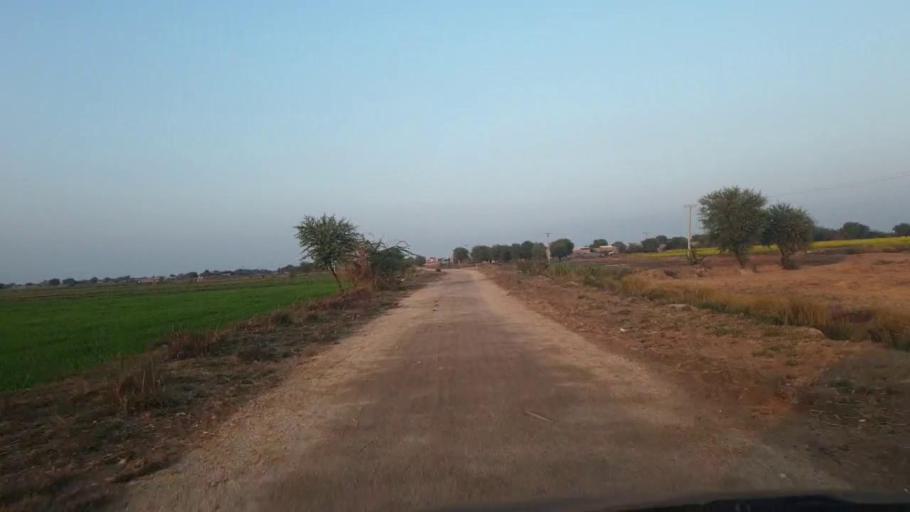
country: PK
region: Sindh
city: Berani
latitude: 25.8274
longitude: 68.7465
